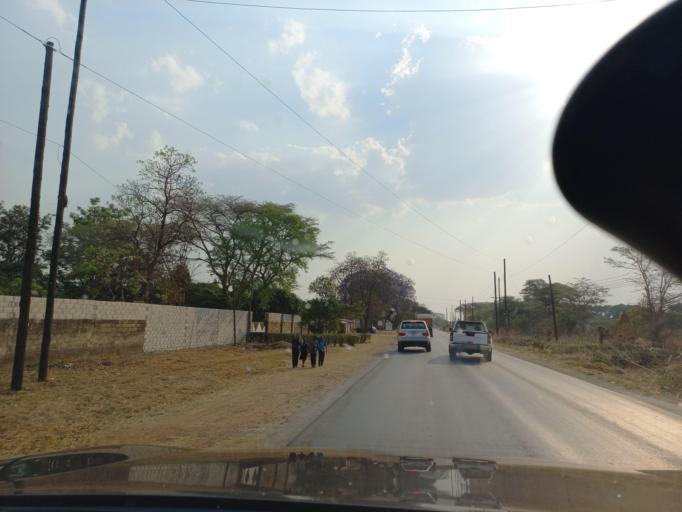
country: ZM
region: Lusaka
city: Lusaka
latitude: -15.4761
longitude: 28.2117
